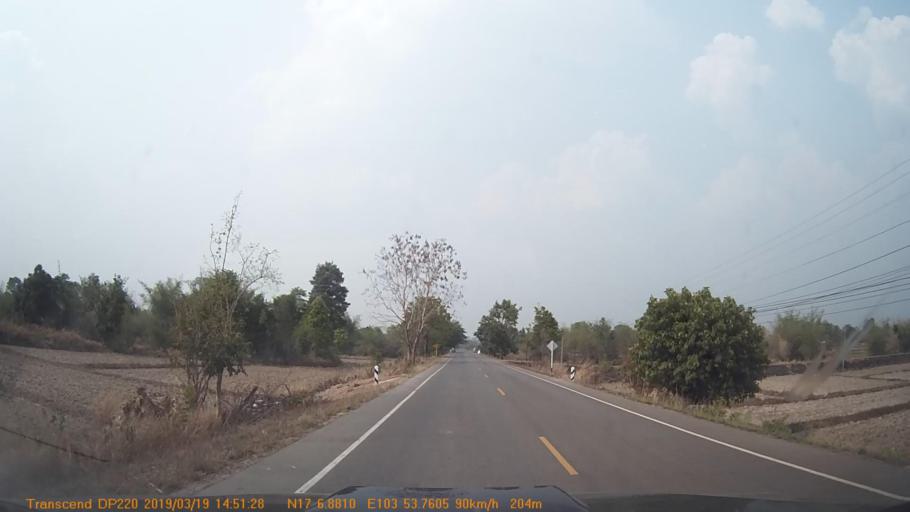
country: TH
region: Sakon Nakhon
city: Kut Bak
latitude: 17.1152
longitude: 103.8960
